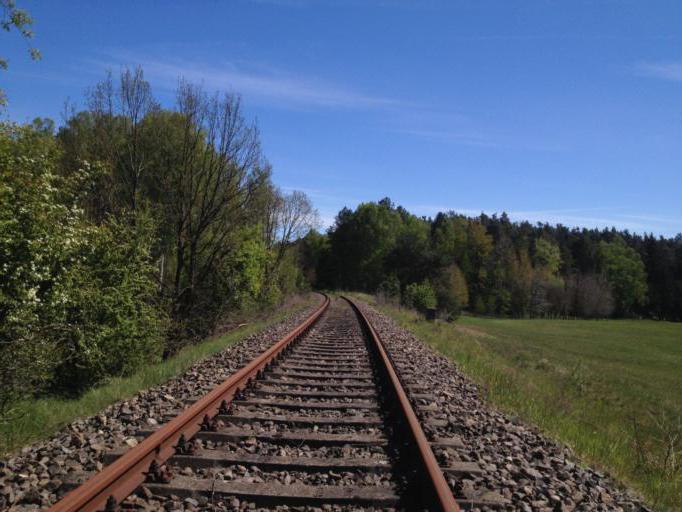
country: DE
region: Brandenburg
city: Lychen
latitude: 53.1537
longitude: 13.3947
